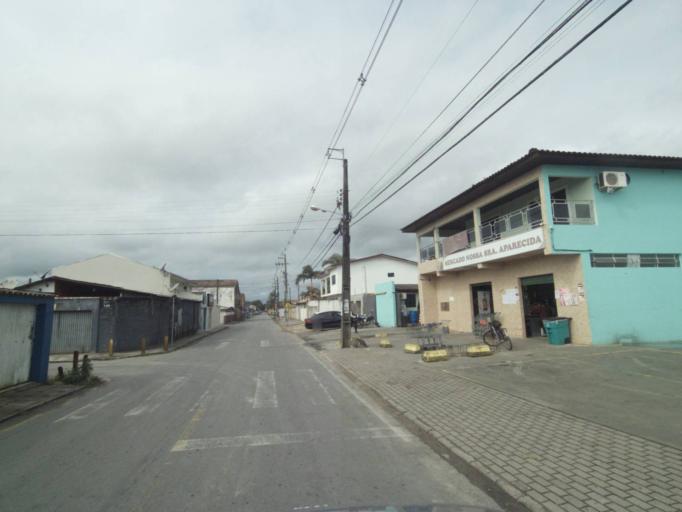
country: BR
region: Parana
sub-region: Paranagua
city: Paranagua
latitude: -25.5657
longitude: -48.5637
